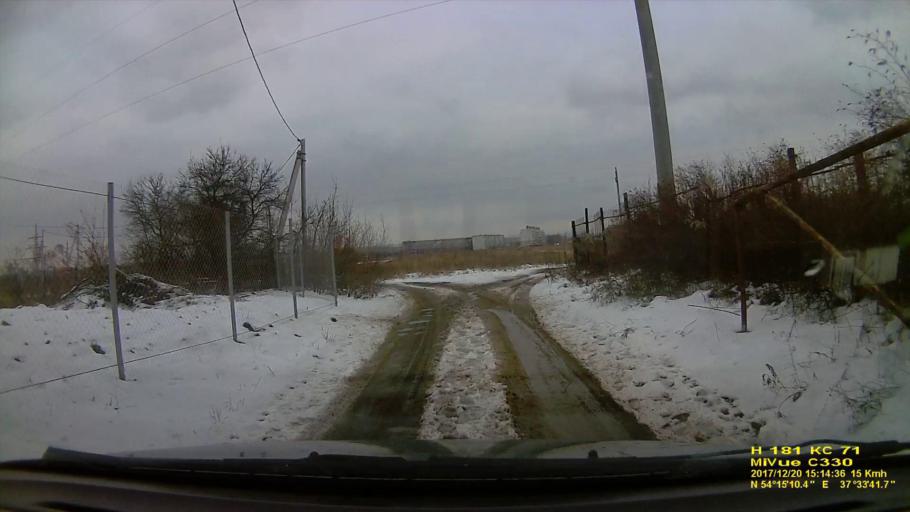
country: RU
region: Tula
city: Gorelki
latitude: 54.2529
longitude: 37.5615
